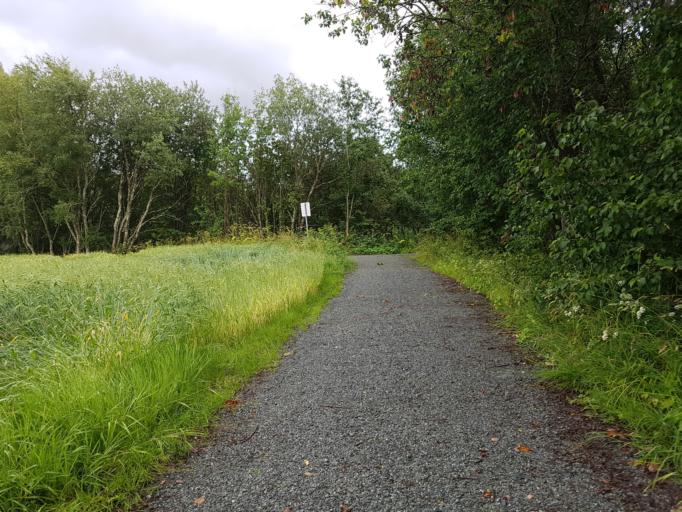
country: NO
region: Sor-Trondelag
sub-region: Trondheim
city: Trondheim
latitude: 63.4089
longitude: 10.4733
